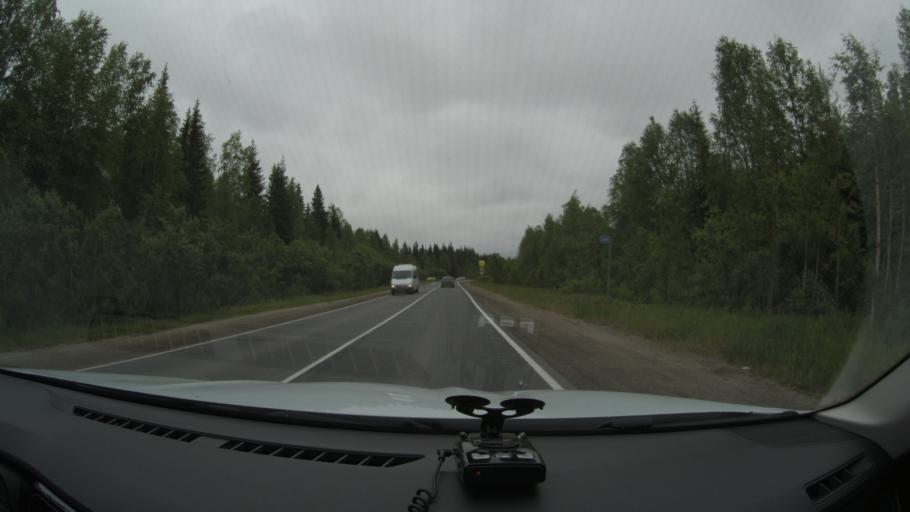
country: RU
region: Komi Republic
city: Shudayag
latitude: 63.5562
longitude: 53.5207
